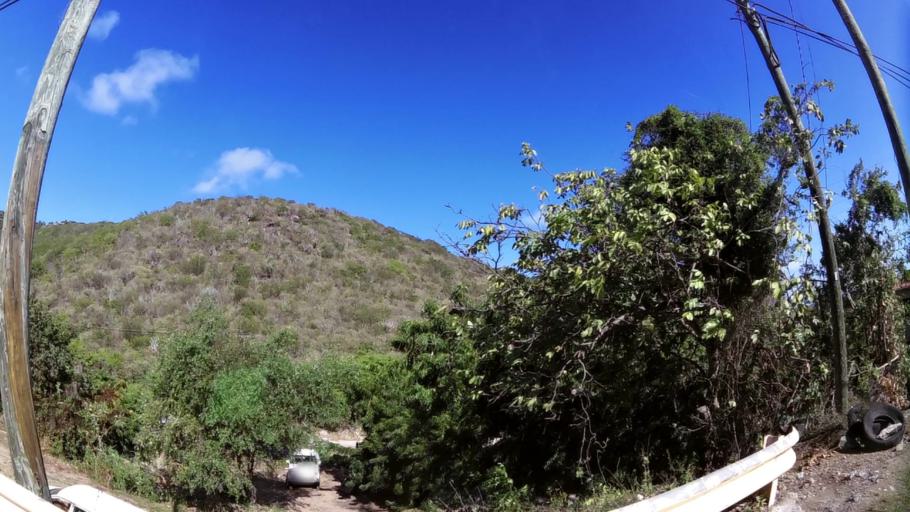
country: VG
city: Tortola
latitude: 18.4881
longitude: -64.3832
